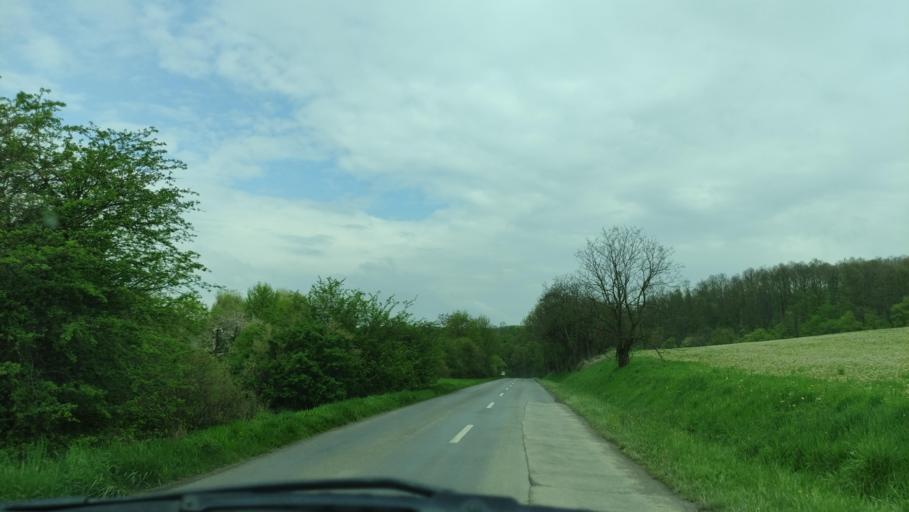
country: HU
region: Baranya
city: Komlo
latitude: 46.2217
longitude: 18.2404
